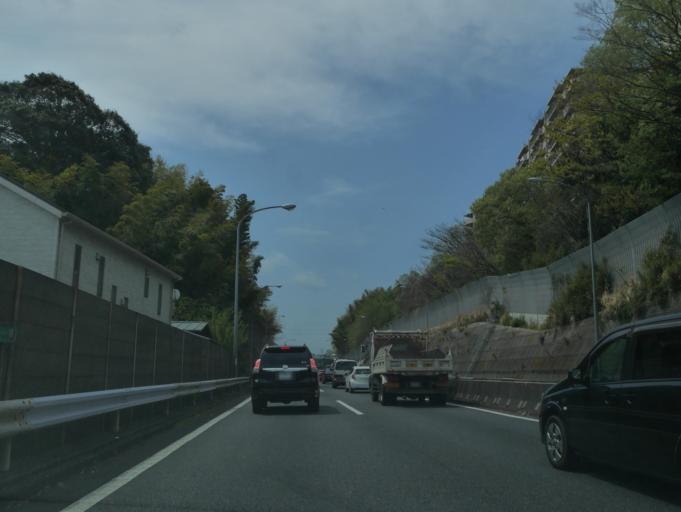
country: JP
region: Kanagawa
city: Fujisawa
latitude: 35.4159
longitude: 139.5364
